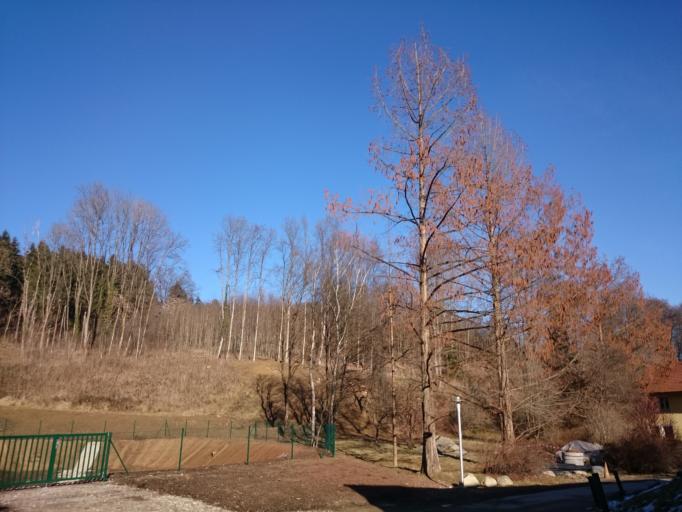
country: AT
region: Styria
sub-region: Graz Stadt
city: Mariatrost
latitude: 47.0892
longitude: 15.4715
